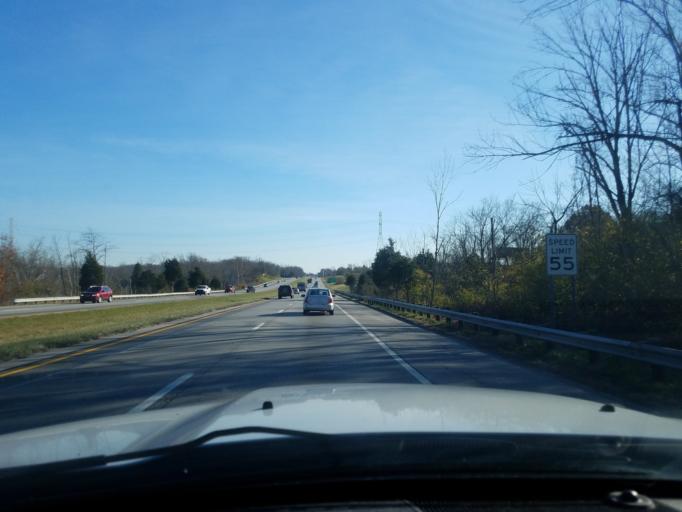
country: US
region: Ohio
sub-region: Clermont County
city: Summerside
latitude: 39.0887
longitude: -84.2338
